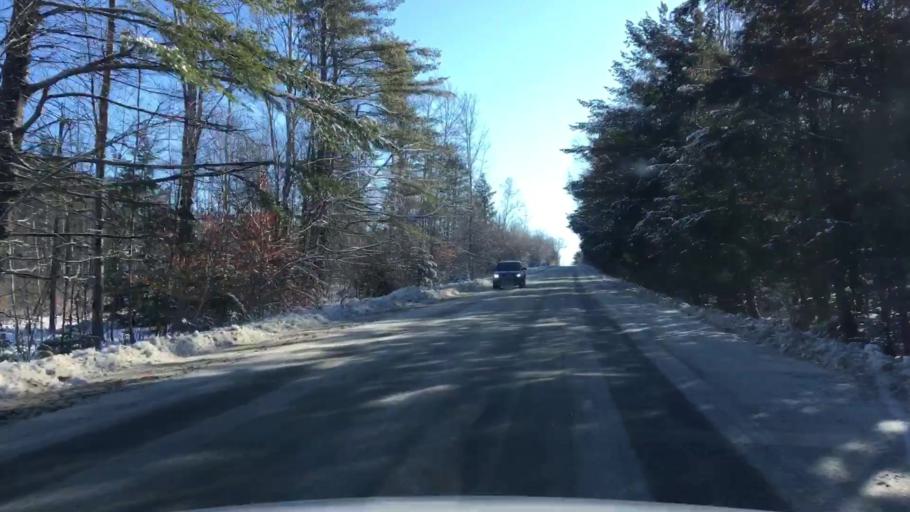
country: US
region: Maine
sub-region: Kennebec County
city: Readfield
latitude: 44.3503
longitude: -69.9906
